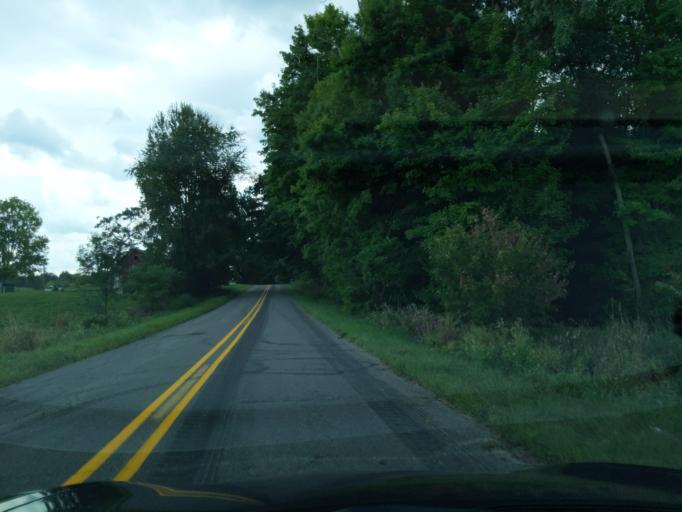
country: US
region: Michigan
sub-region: Eaton County
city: Eaton Rapids
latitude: 42.4139
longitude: -84.5808
